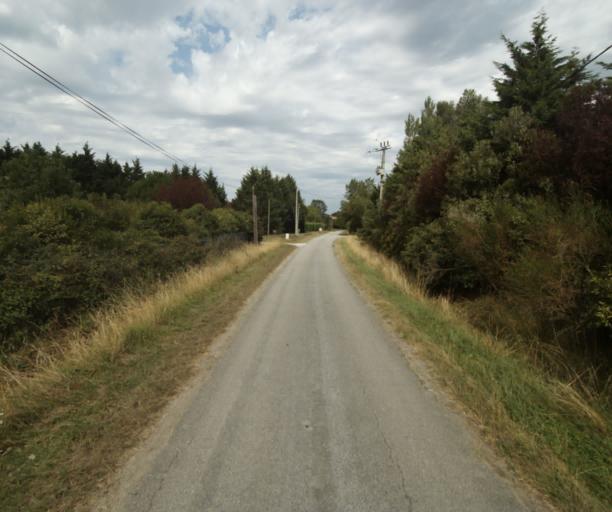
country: FR
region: Midi-Pyrenees
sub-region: Departement de la Haute-Garonne
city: Saint-Felix-Lauragais
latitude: 43.4317
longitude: 1.9424
